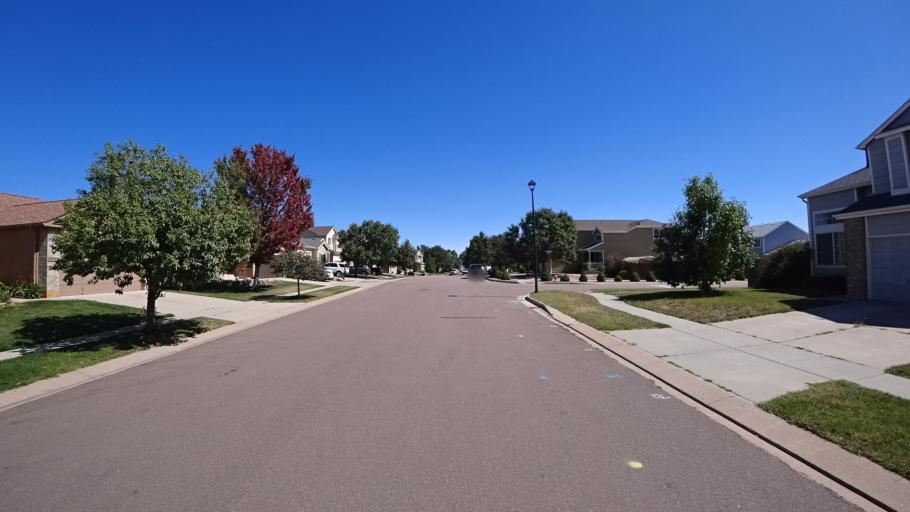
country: US
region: Colorado
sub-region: El Paso County
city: Security-Widefield
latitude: 38.7854
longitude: -104.7320
